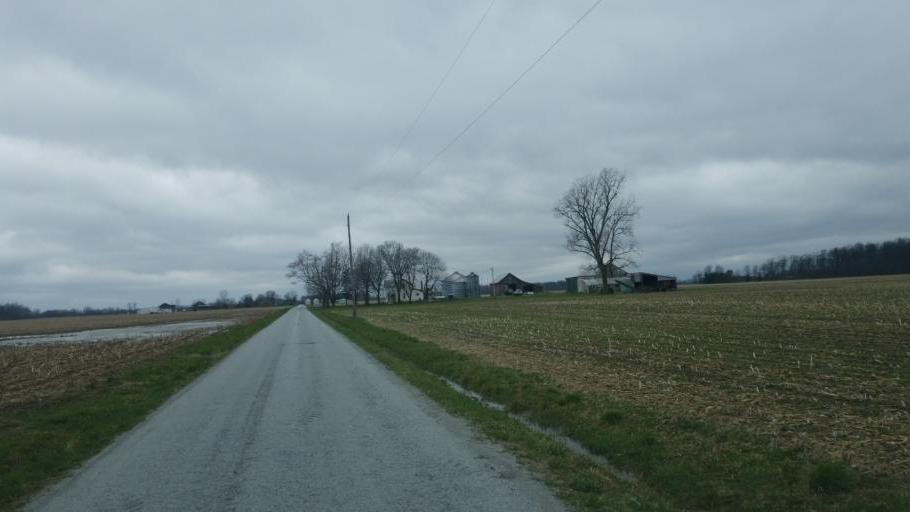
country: US
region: Ohio
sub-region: Hardin County
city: Forest
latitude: 40.7307
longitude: -83.5393
